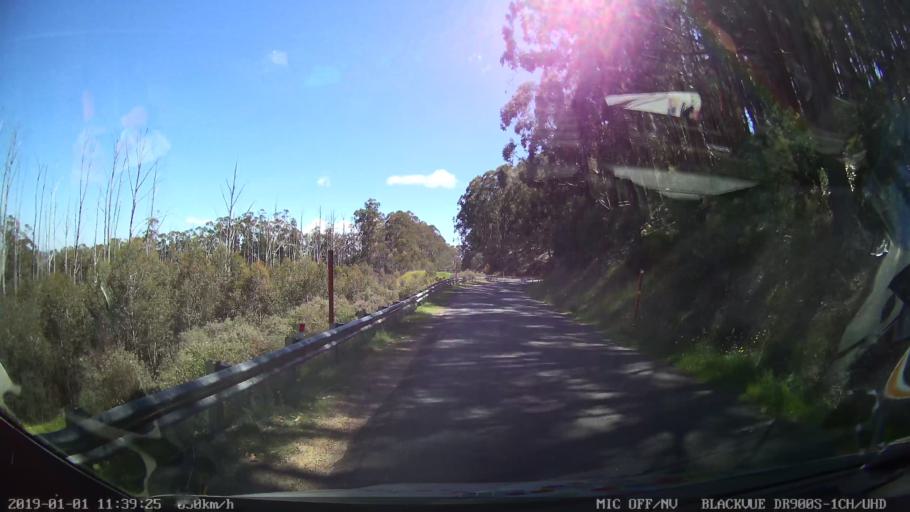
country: AU
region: New South Wales
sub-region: Snowy River
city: Jindabyne
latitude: -35.9267
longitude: 148.3864
